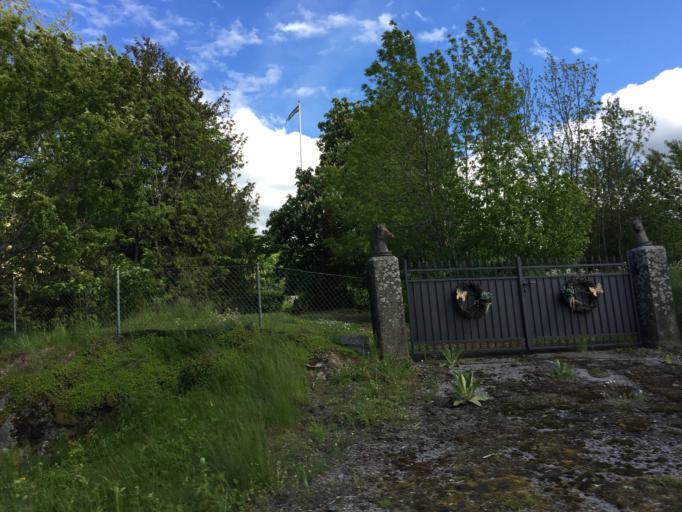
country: SE
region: OEstergoetland
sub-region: Norrkopings Kommun
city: Skarblacka
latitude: 58.5806
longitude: 15.8141
